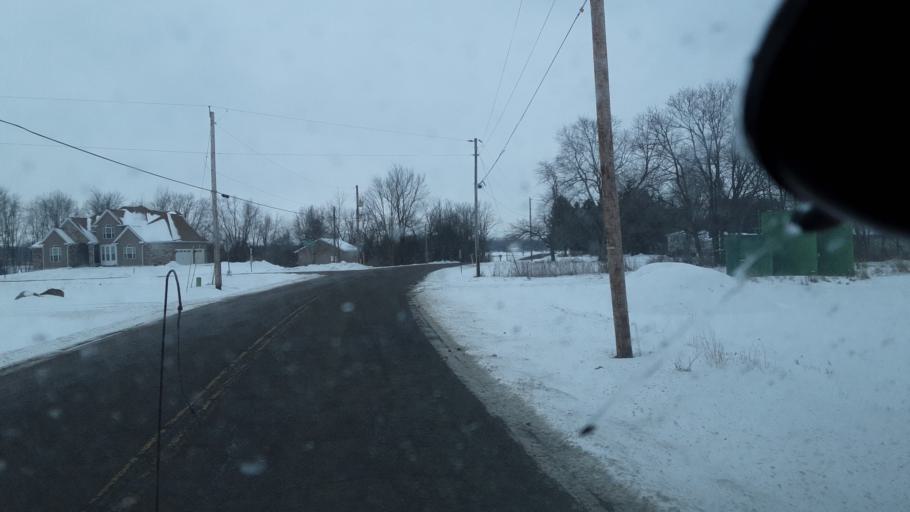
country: US
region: Ohio
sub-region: Licking County
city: Hebron
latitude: 39.9701
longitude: -82.4567
